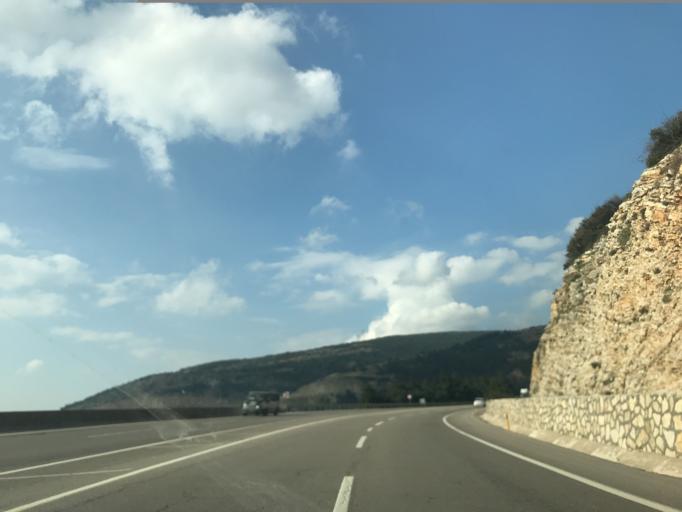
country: TR
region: Hatay
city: Belen
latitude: 36.4754
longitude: 36.2447
